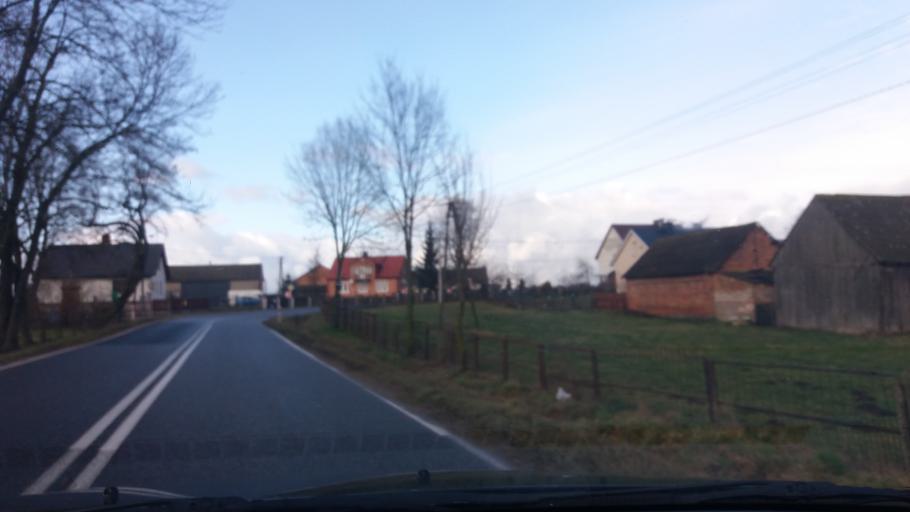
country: PL
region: Masovian Voivodeship
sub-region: Powiat przasnyski
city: Chorzele
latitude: 53.2350
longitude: 20.8807
